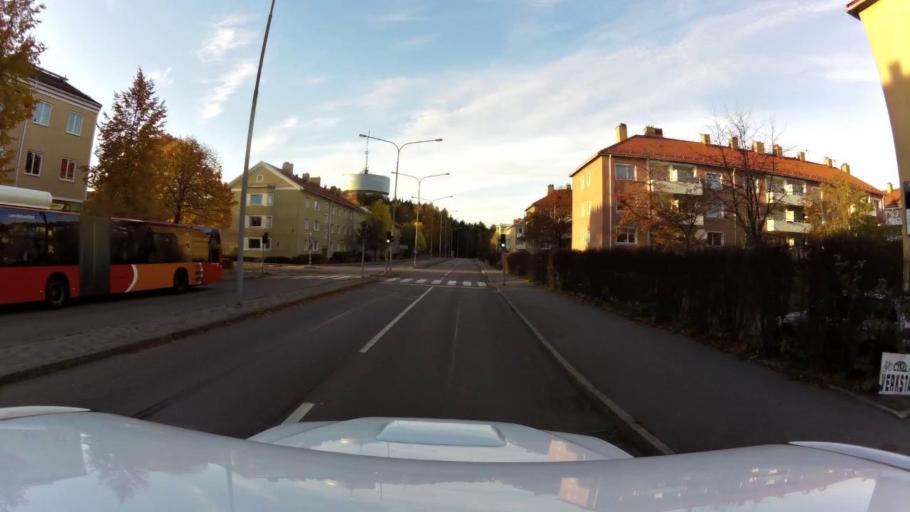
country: SE
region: OEstergoetland
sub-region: Linkopings Kommun
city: Linkoping
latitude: 58.3975
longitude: 15.6387
